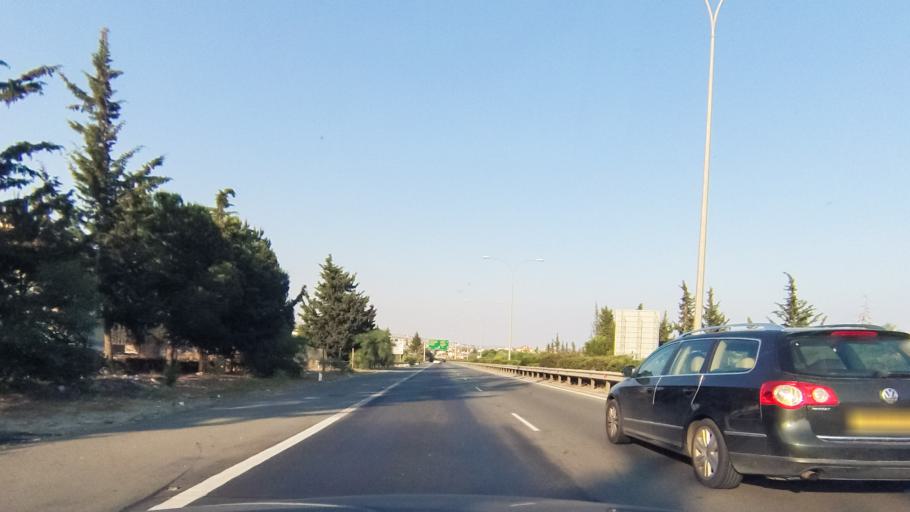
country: CY
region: Limassol
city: Mouttagiaka
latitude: 34.7090
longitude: 33.0719
